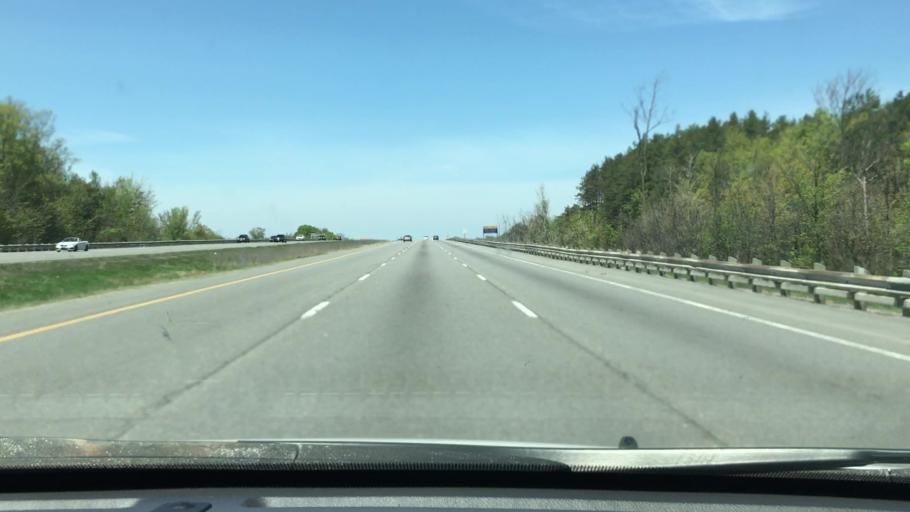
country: CA
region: Ontario
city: Newmarket
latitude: 43.9876
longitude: -79.3948
